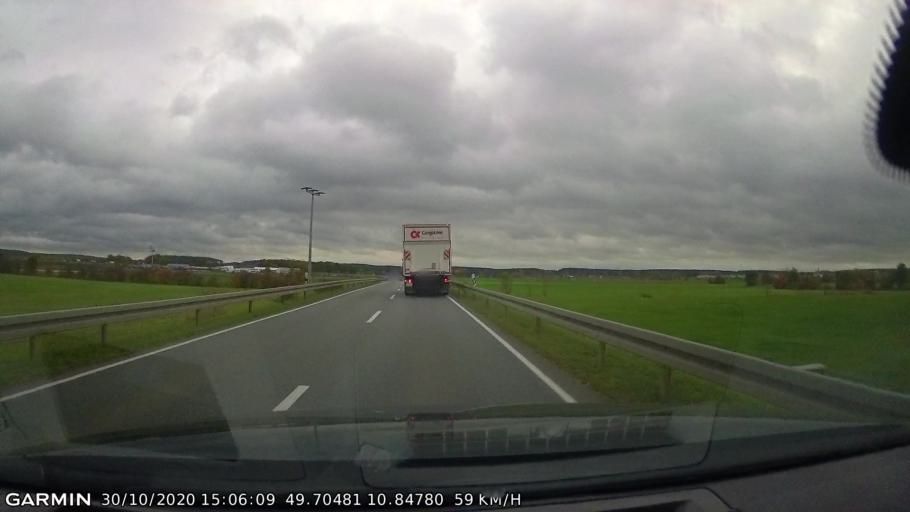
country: DE
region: Bavaria
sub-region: Regierungsbezirk Mittelfranken
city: Gremsdorf
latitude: 49.7048
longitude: 10.8480
